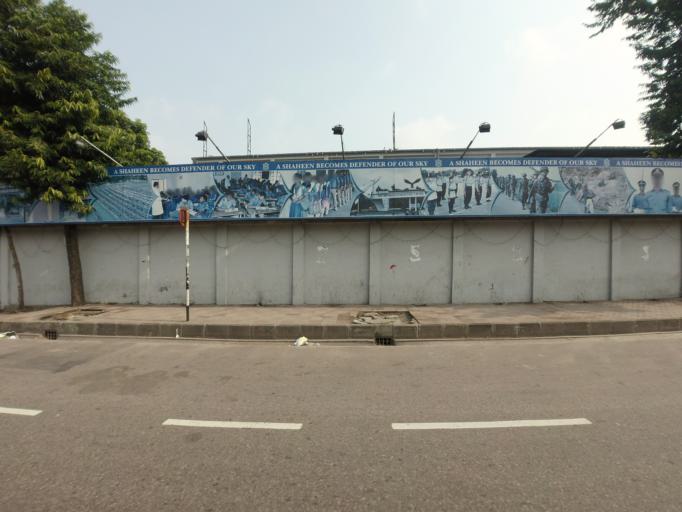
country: BD
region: Dhaka
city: Paltan
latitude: 23.7757
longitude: 90.3914
